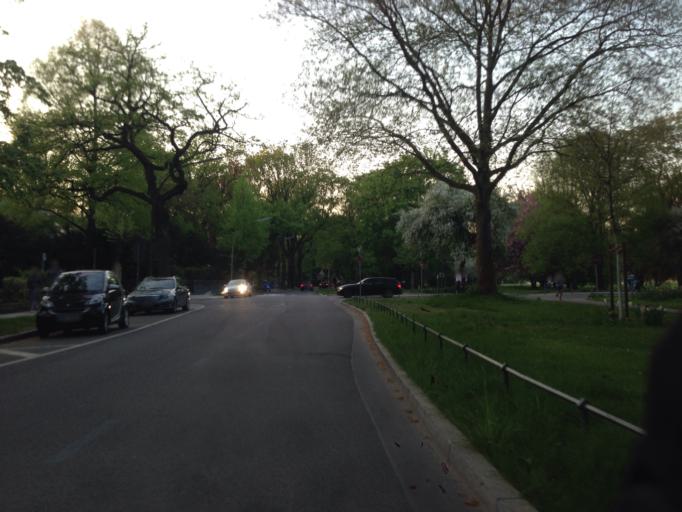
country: DE
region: Hamburg
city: Hamburg
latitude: 53.5729
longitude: 9.9995
